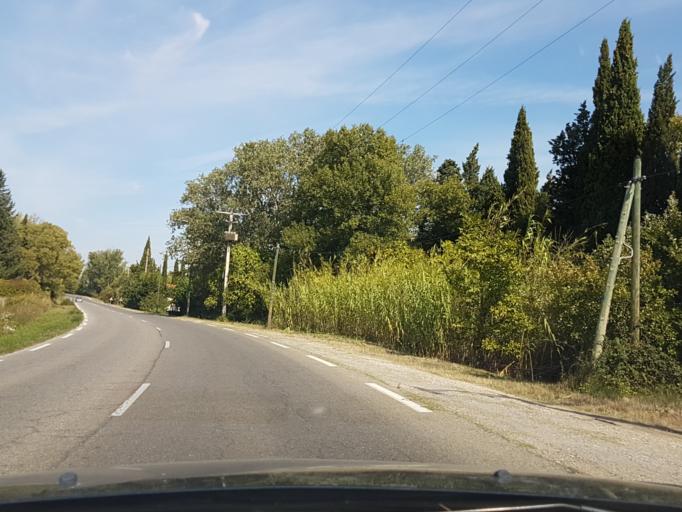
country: FR
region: Provence-Alpes-Cote d'Azur
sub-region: Departement des Bouches-du-Rhone
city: Saint-Remy-de-Provence
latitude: 43.8029
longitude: 4.8609
